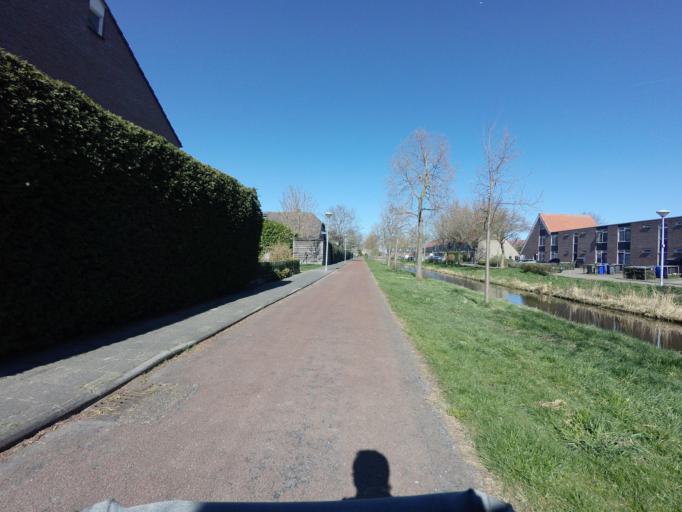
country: NL
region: Utrecht
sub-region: Gemeente Woerden
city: Woerden
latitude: 52.0810
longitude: 4.8569
